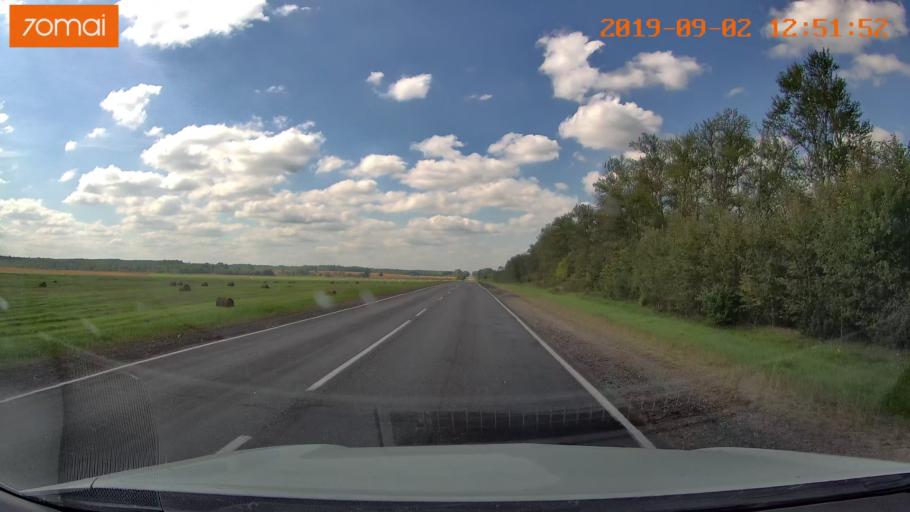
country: BY
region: Mogilev
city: Klimavichy
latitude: 53.7286
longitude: 32.1116
